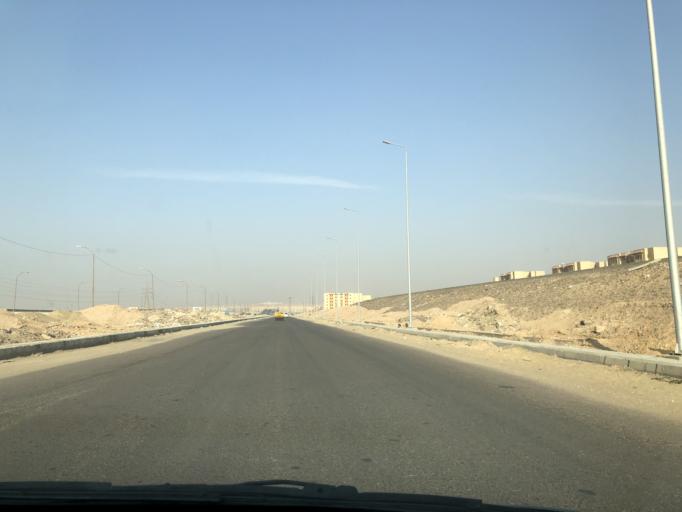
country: EG
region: Al Jizah
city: Madinat Sittah Uktubar
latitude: 29.9030
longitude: 30.9143
